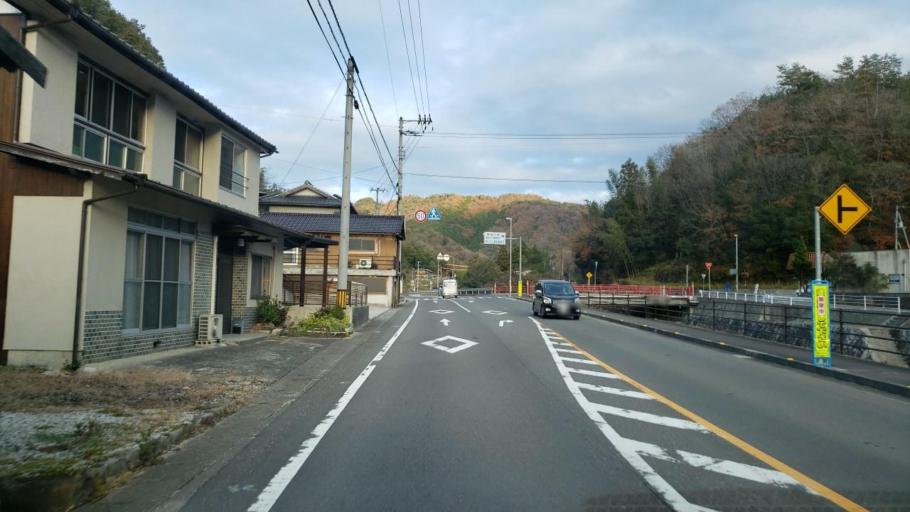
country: JP
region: Tokushima
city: Wakimachi
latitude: 34.1712
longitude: 134.0957
